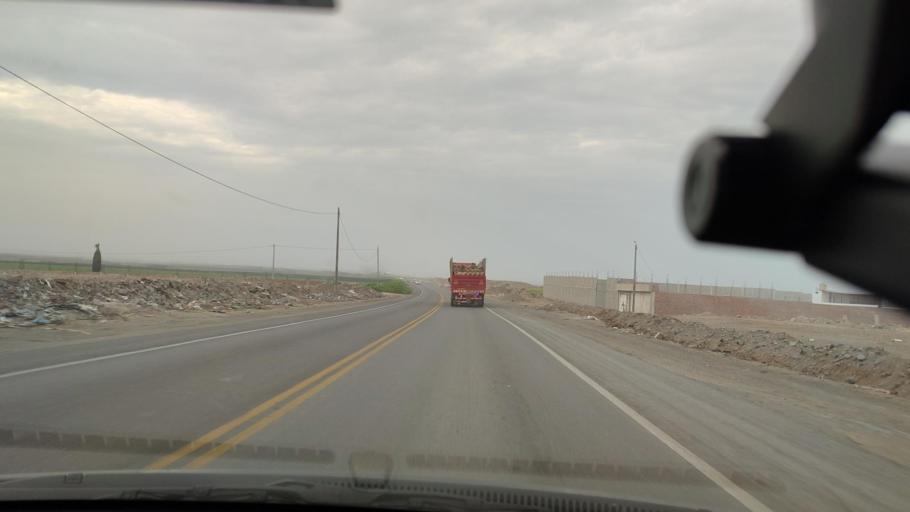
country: PE
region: La Libertad
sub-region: Provincia de Trujillo
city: Huanchaco
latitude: -8.1061
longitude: -79.0980
